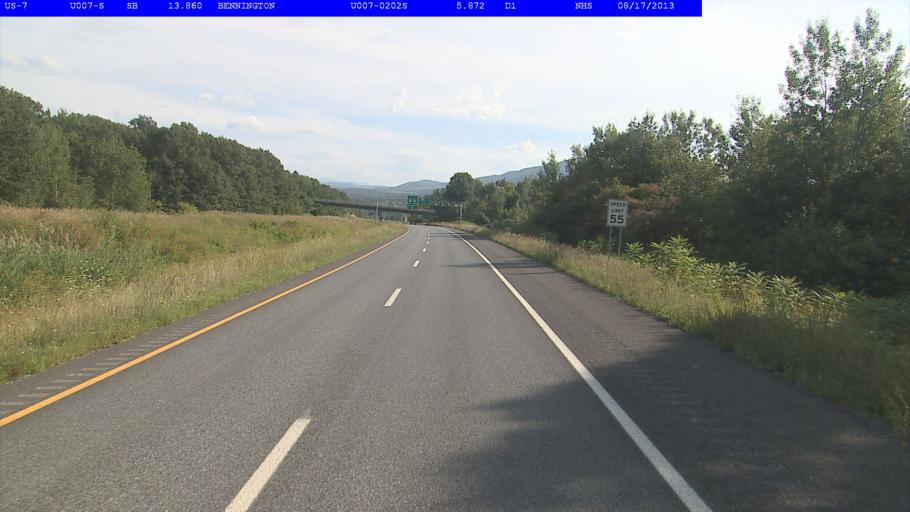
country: US
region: Vermont
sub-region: Bennington County
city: North Bennington
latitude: 42.9171
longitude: -73.2085
